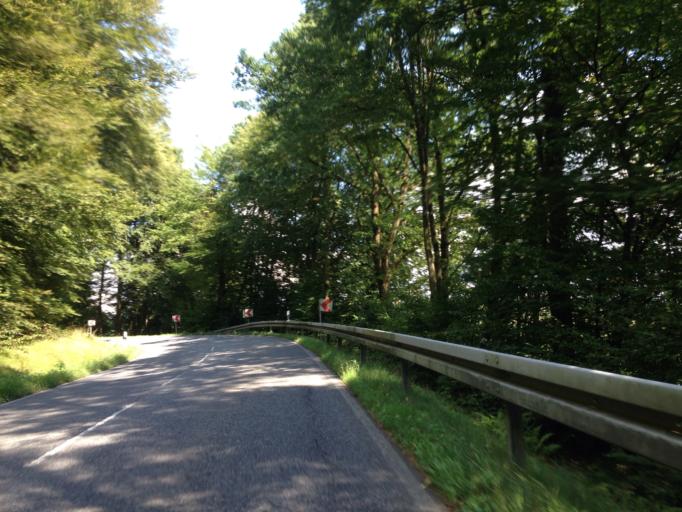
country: DE
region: Hesse
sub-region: Regierungsbezirk Giessen
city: Lohnberg
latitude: 50.5352
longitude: 8.2335
